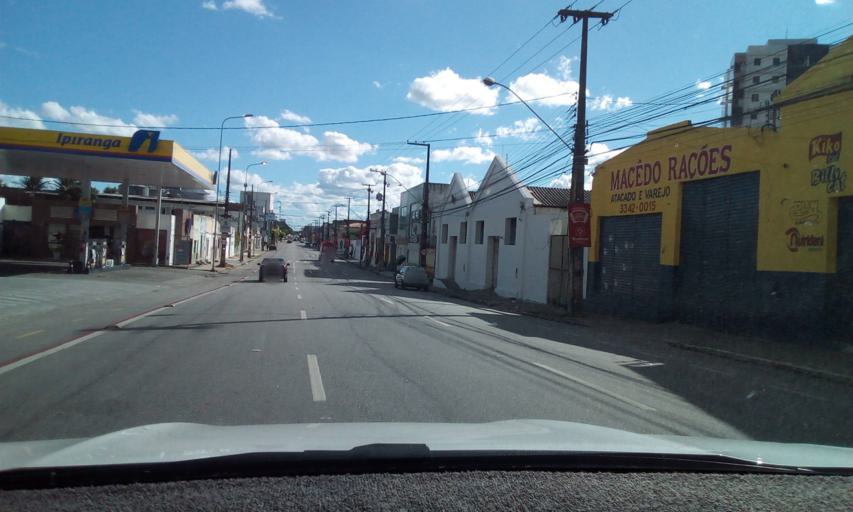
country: BR
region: Paraiba
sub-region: Campina Grande
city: Campina Grande
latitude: -7.2274
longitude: -35.8858
